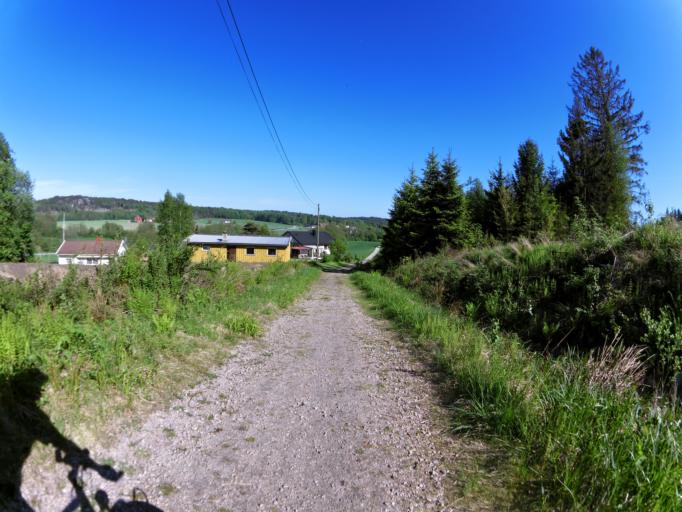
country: NO
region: Ostfold
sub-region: Sarpsborg
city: Sarpsborg
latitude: 59.2231
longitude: 11.0534
